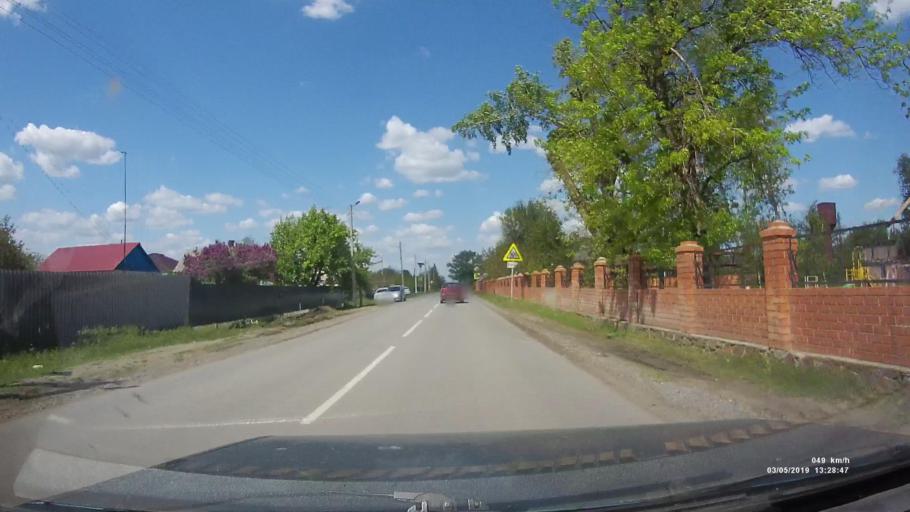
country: RU
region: Rostov
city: Semikarakorsk
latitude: 47.5785
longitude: 40.8417
